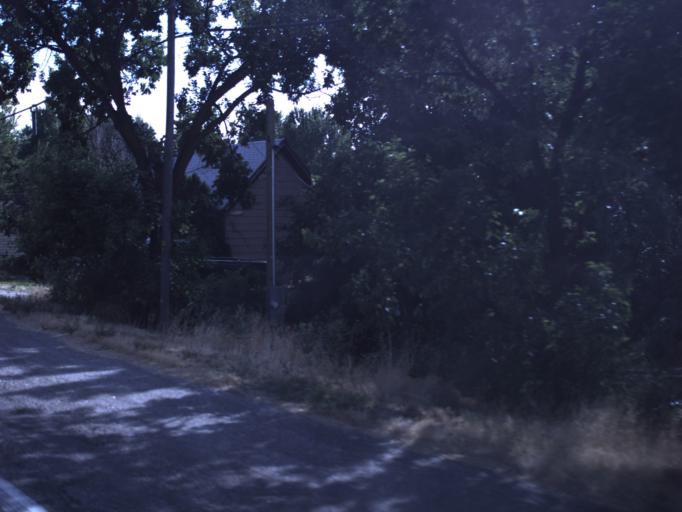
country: US
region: Utah
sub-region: Box Elder County
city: Willard
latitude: 41.4152
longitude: -112.0362
